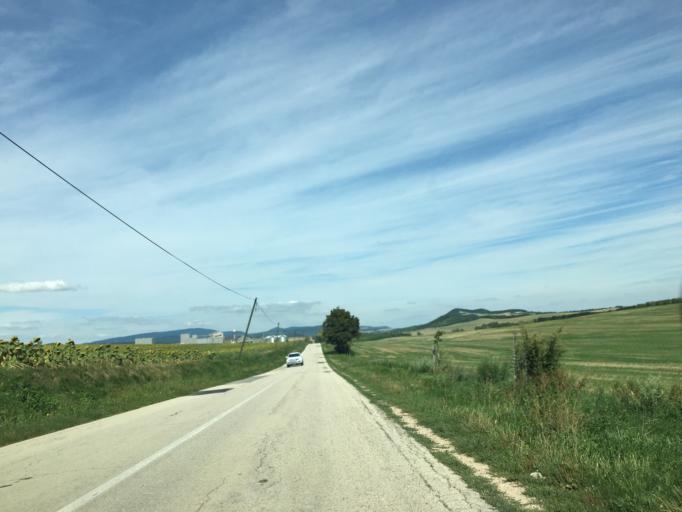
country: HU
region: Fejer
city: Many
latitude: 47.6002
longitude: 18.6542
